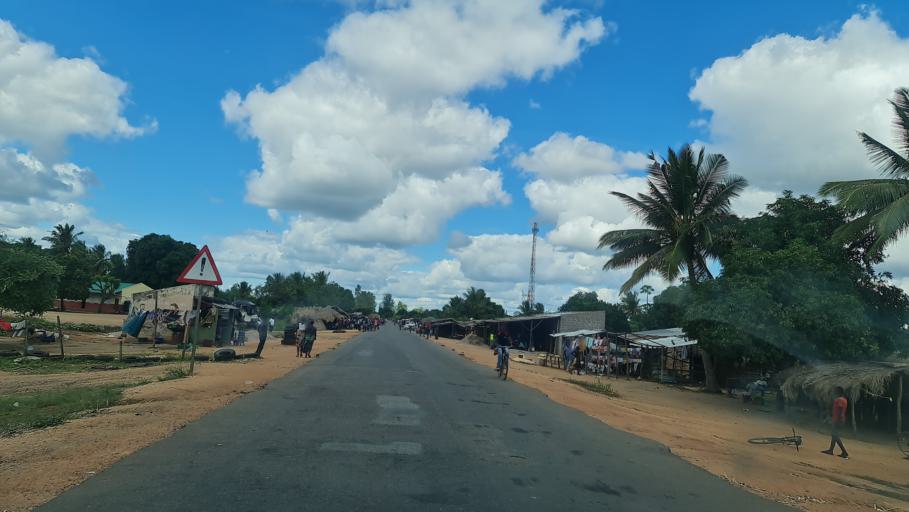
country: MZ
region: Zambezia
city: Quelimane
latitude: -17.5206
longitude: 36.2648
